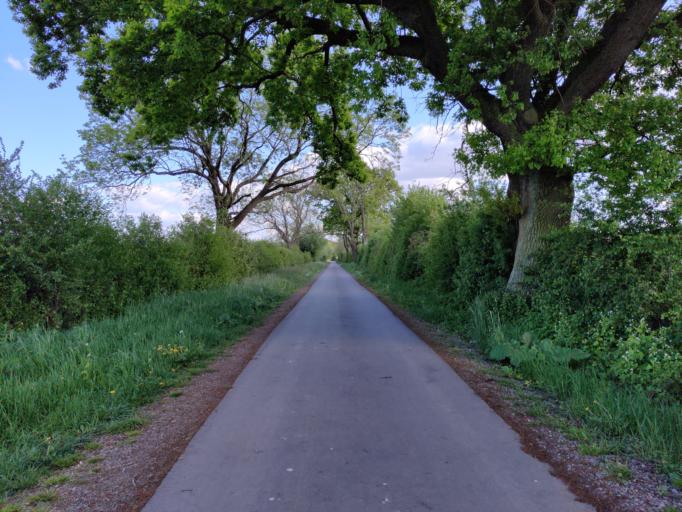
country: DE
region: Lower Saxony
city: Wunstorf
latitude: 52.4419
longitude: 9.4745
